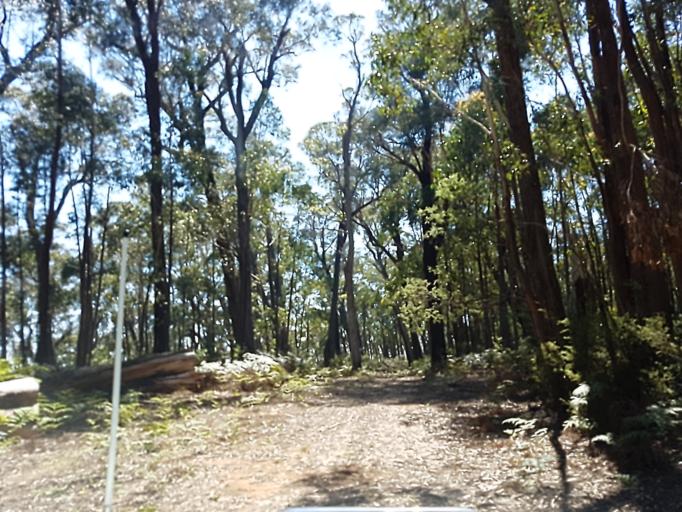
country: AU
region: Victoria
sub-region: East Gippsland
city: Lakes Entrance
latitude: -37.2906
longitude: 148.3211
